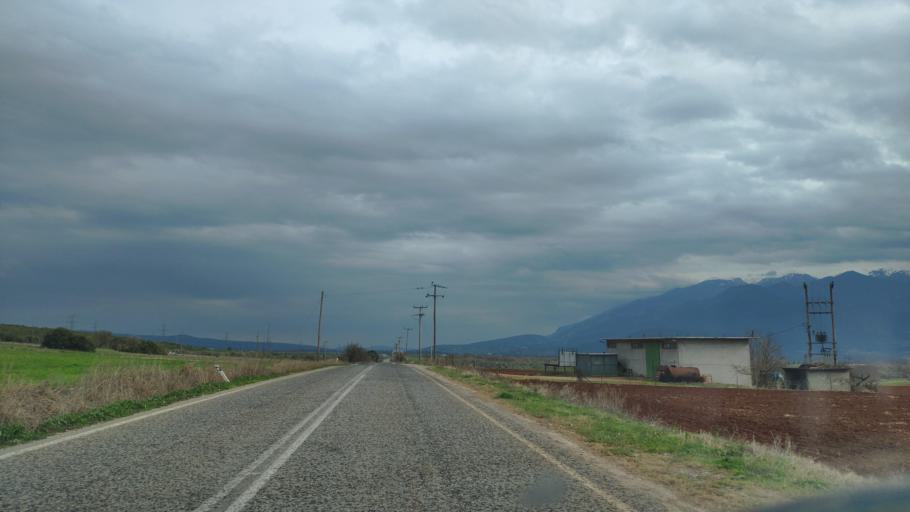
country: GR
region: Central Greece
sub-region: Nomos Fthiotidos
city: Amfikleia
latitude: 38.7043
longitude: 22.5062
